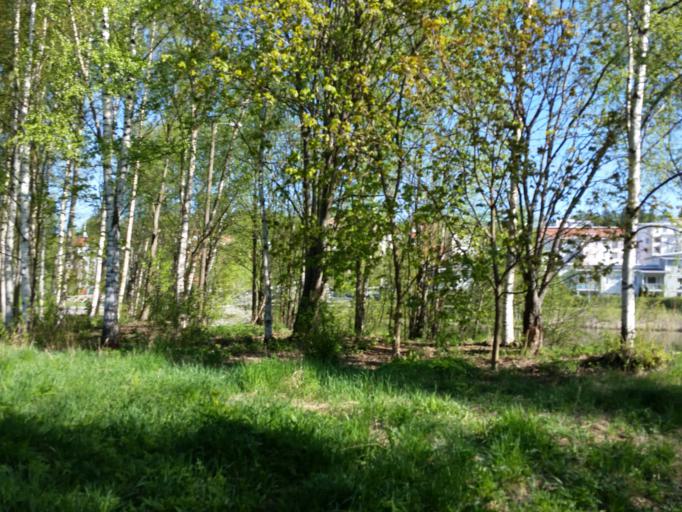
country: FI
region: Pirkanmaa
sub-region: Tampere
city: Tampere
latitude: 61.4888
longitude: 23.7869
